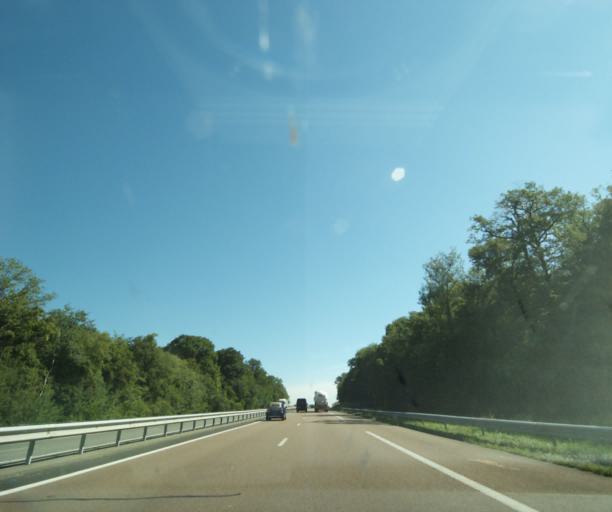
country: FR
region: Champagne-Ardenne
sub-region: Departement de la Haute-Marne
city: Saulxures
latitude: 48.0625
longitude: 5.5868
